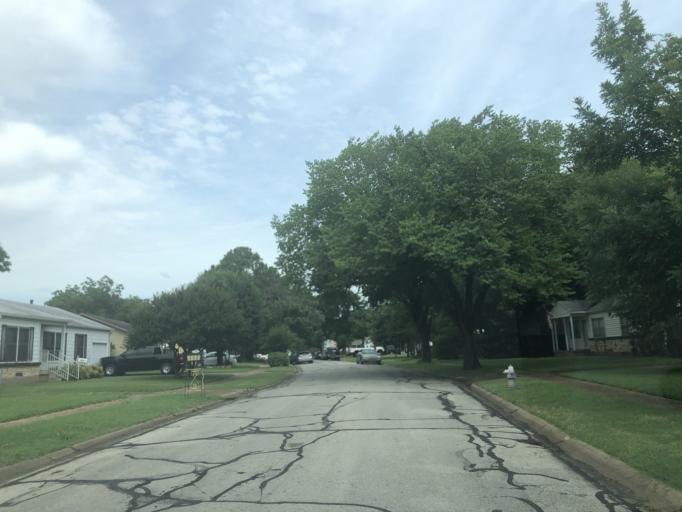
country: US
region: Texas
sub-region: Dallas County
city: Irving
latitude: 32.8020
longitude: -96.9483
